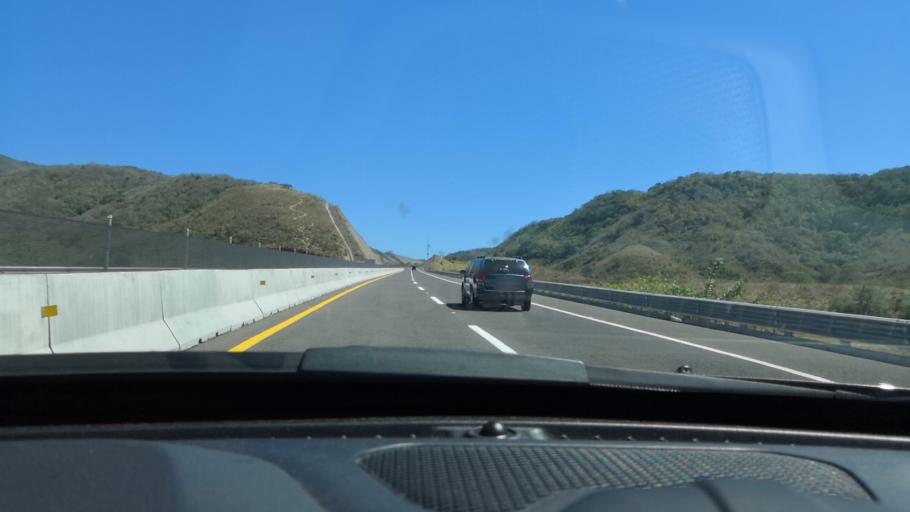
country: MX
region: Nayarit
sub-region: Compostela
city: Juan Escutia (Borbollon)
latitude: 21.1343
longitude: -104.9095
